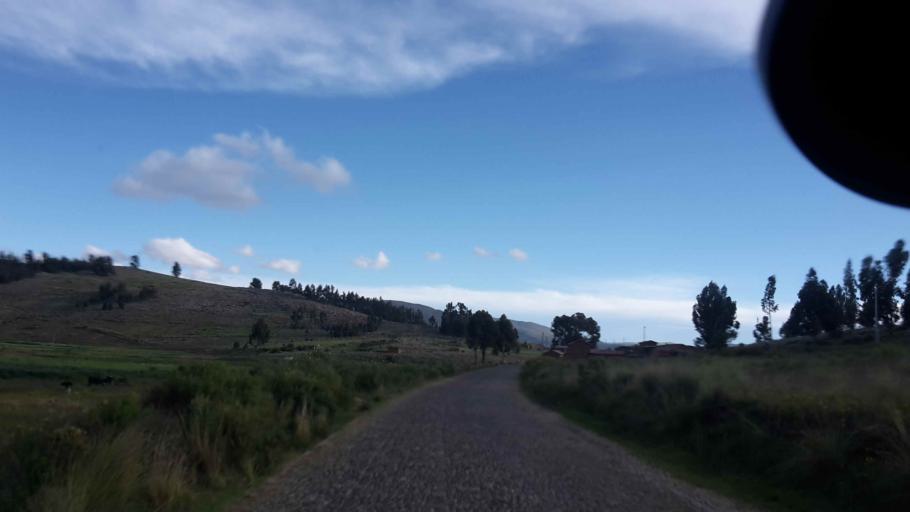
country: BO
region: Cochabamba
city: Arani
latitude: -17.5387
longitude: -65.6616
